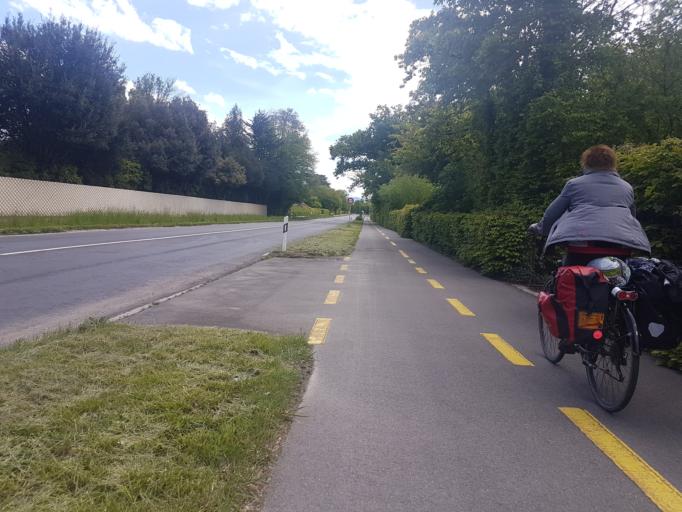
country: CH
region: Vaud
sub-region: Nyon District
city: Founex
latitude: 46.3463
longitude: 6.2062
